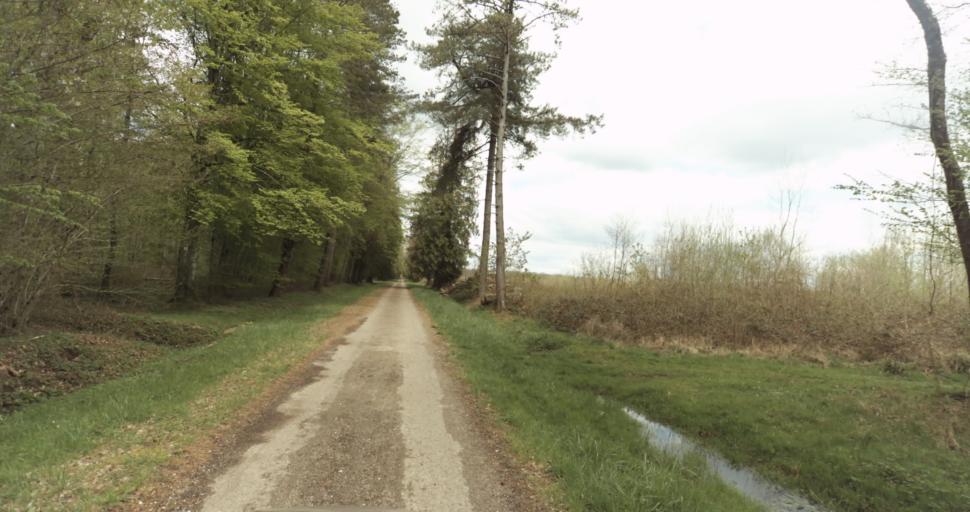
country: FR
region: Bourgogne
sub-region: Departement de la Cote-d'Or
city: Auxonne
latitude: 47.1591
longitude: 5.4227
